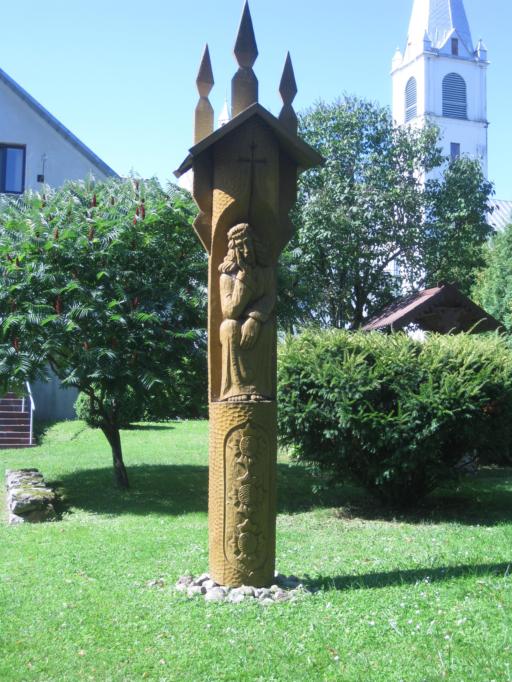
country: LT
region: Kauno apskritis
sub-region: Kauno rajonas
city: Garliava
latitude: 54.7367
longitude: 23.9234
